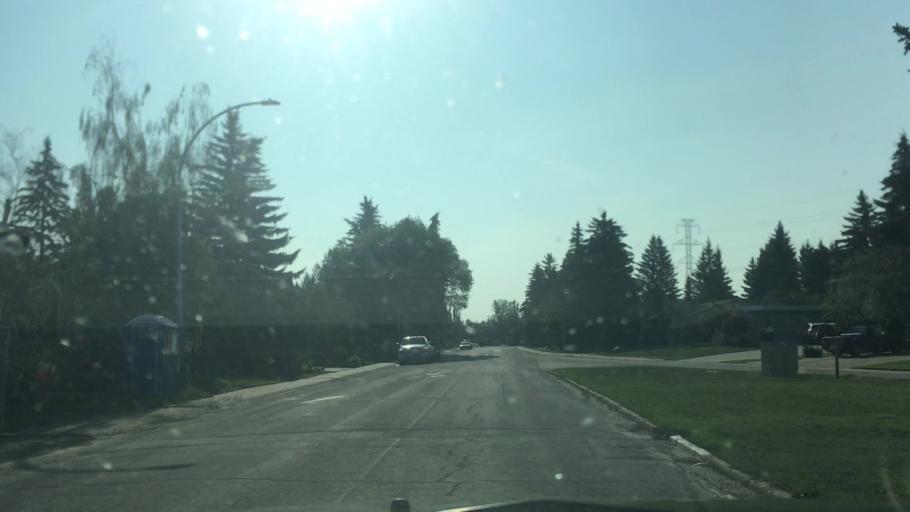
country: CA
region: Alberta
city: Edmonton
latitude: 53.4627
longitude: -113.5421
